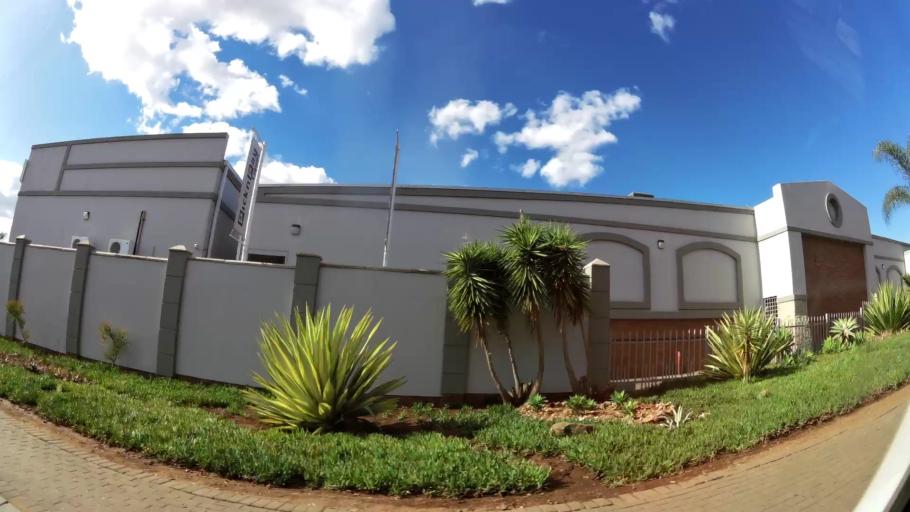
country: ZA
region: Limpopo
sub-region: Capricorn District Municipality
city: Polokwane
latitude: -23.8932
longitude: 29.4722
